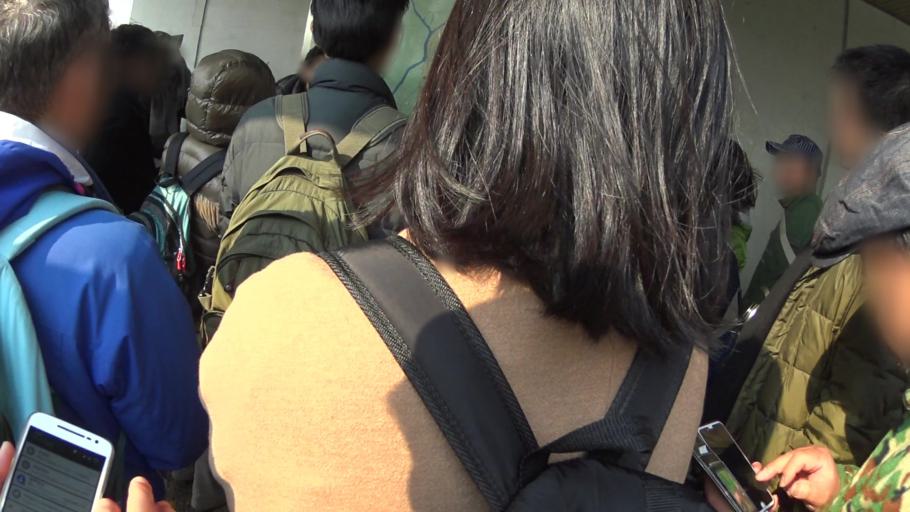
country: JP
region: Ibaraki
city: Koga
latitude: 36.1810
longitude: 139.6982
